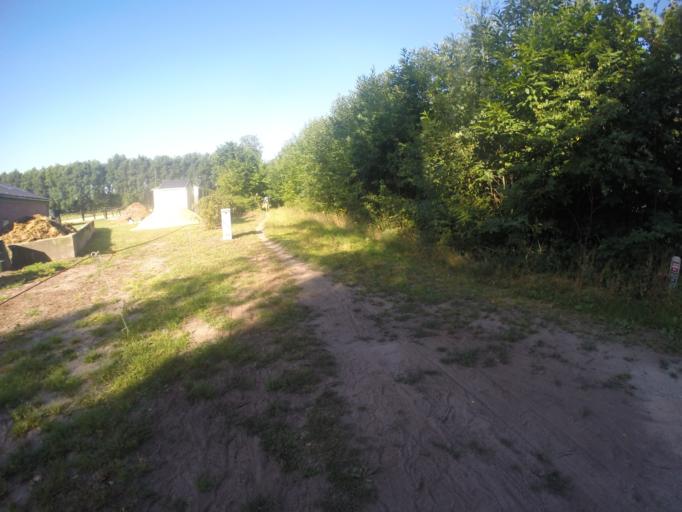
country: NL
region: Gelderland
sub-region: Gemeente Lochem
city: Almen
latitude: 52.1181
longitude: 6.3431
